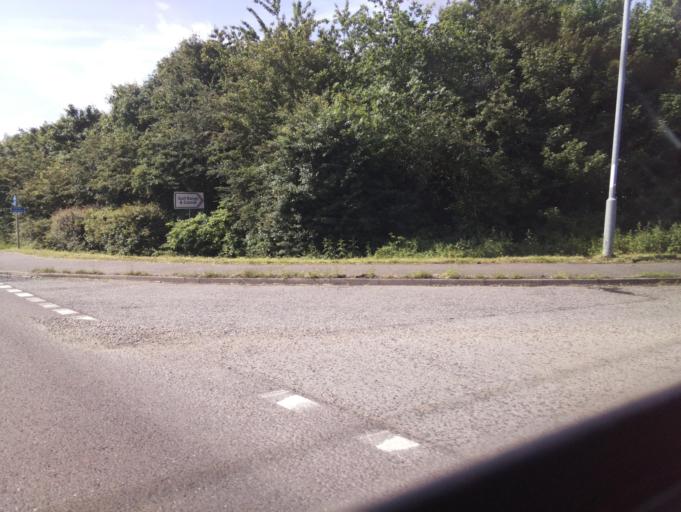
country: GB
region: England
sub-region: Lincolnshire
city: Skellingthorpe
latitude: 53.1828
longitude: -0.6272
